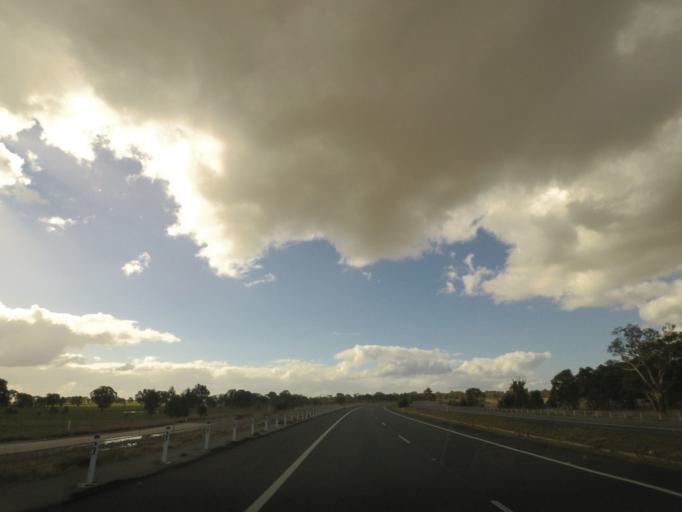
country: AU
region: New South Wales
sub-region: Greater Hume Shire
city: Holbrook
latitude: -35.7130
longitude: 147.3039
